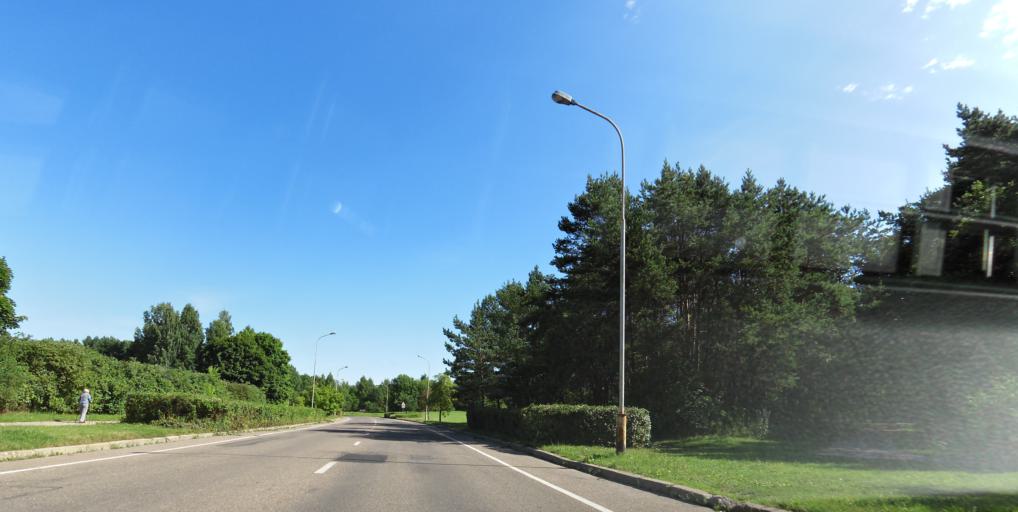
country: LT
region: Vilnius County
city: Justiniskes
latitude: 54.6982
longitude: 25.2301
